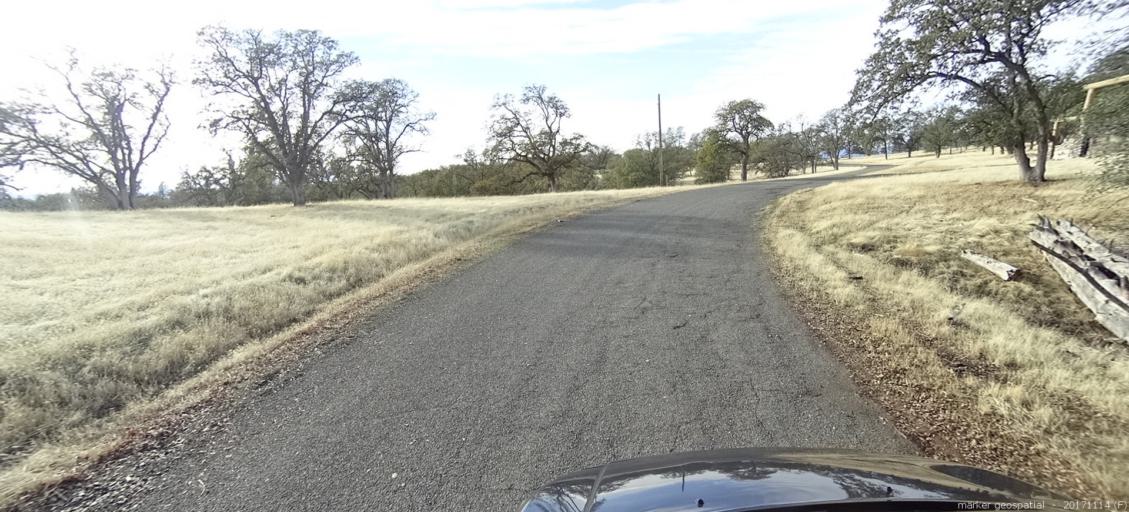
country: US
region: California
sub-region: Shasta County
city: Shasta
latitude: 40.3834
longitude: -122.5845
